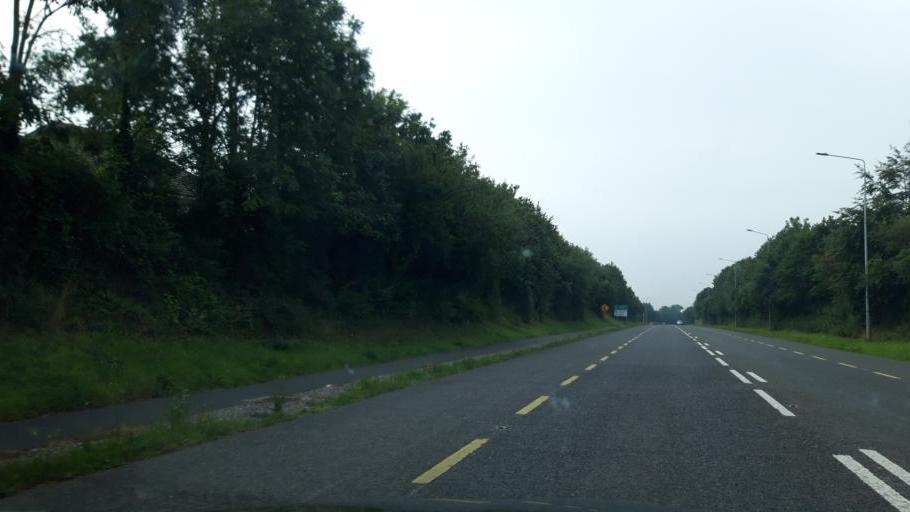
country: IE
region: Leinster
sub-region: Kilkenny
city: Callan
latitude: 52.5420
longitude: -7.3969
